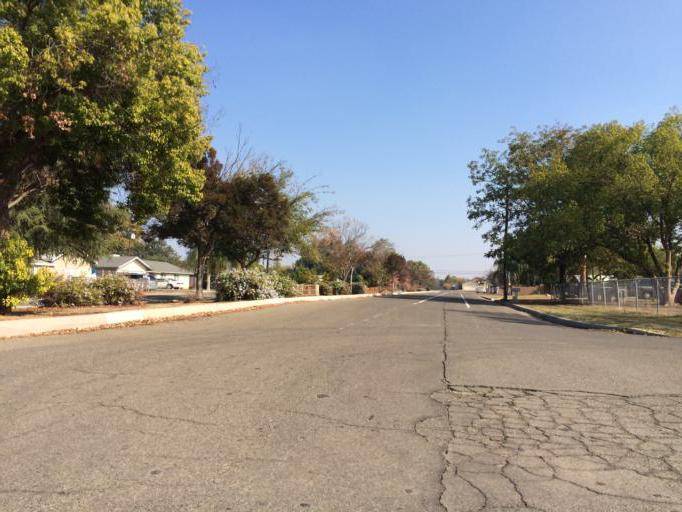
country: US
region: California
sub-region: Fresno County
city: Sunnyside
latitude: 36.7468
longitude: -119.7297
